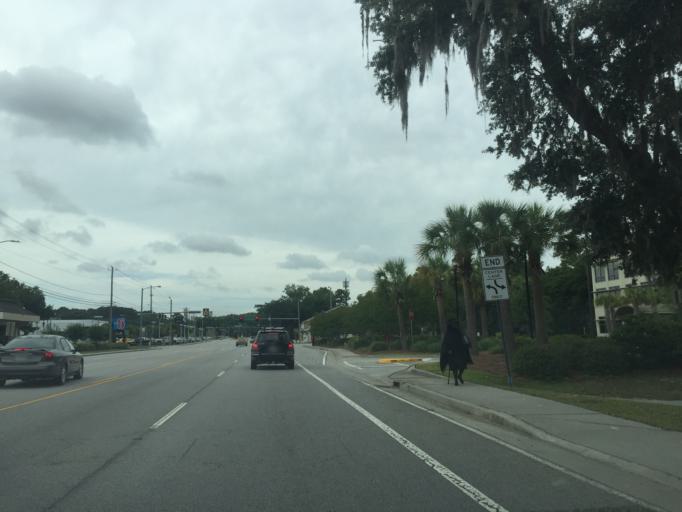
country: US
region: Georgia
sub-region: Chatham County
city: Isle of Hope
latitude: 32.0130
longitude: -81.1099
